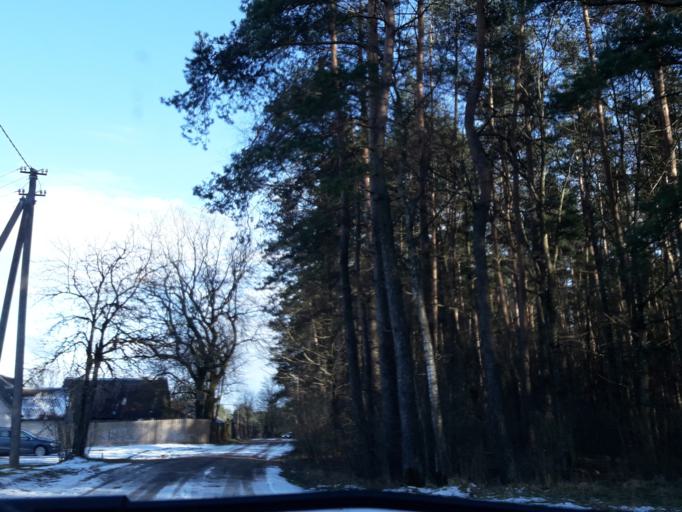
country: LV
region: Kekava
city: Kekava
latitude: 56.8461
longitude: 24.1908
